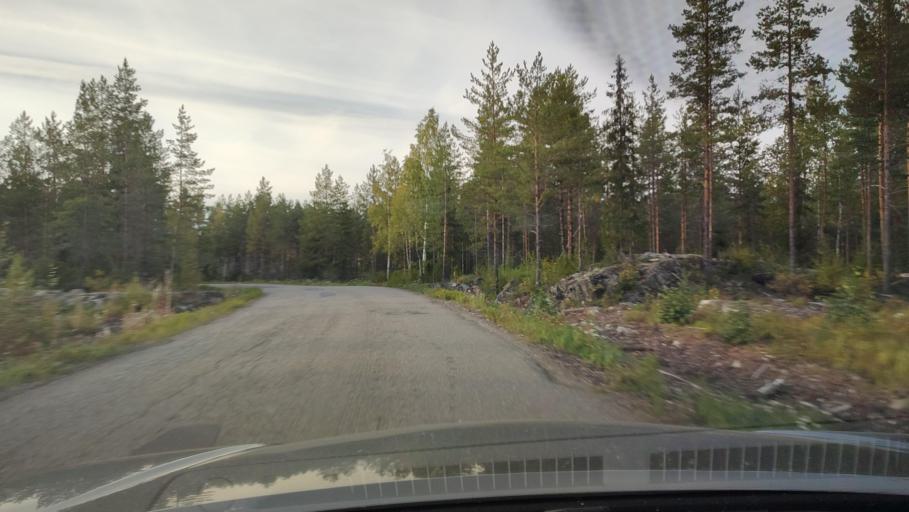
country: FI
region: Ostrobothnia
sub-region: Sydosterbotten
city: Kristinestad
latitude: 62.1489
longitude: 21.5530
